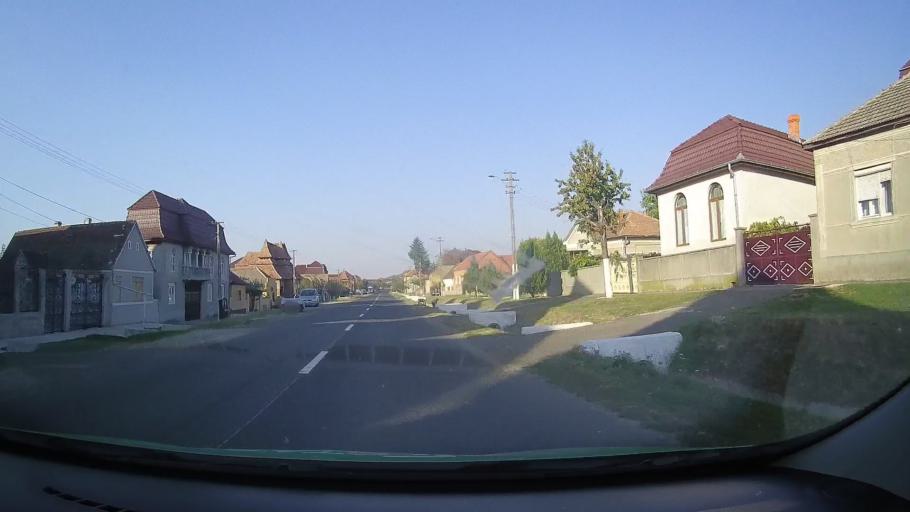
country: RO
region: Arad
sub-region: Comuna Covasint
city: Covasint
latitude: 46.1935
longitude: 21.6061
